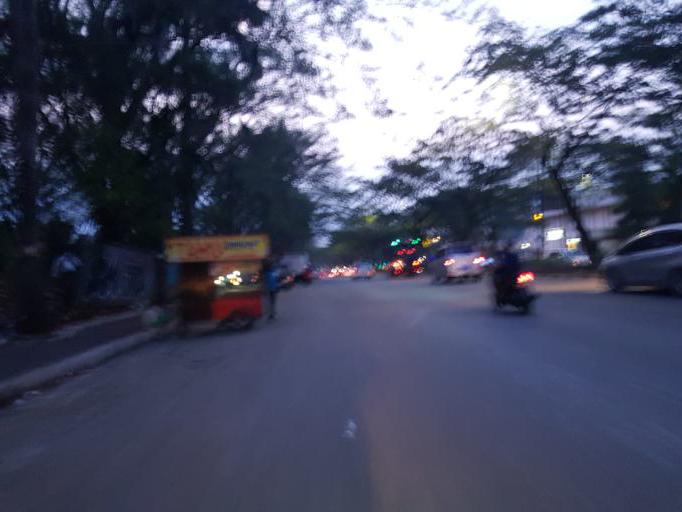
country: ID
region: West Java
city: Serpong
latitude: -6.3279
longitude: 106.6845
